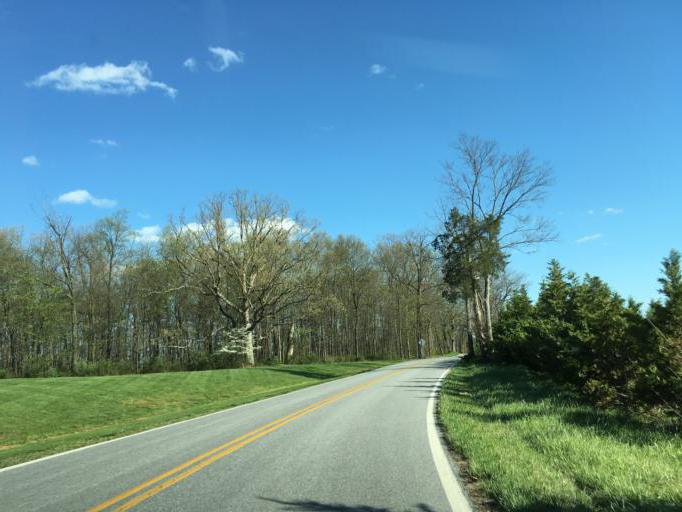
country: US
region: Maryland
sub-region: Frederick County
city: Emmitsburg
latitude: 39.6374
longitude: -77.2882
